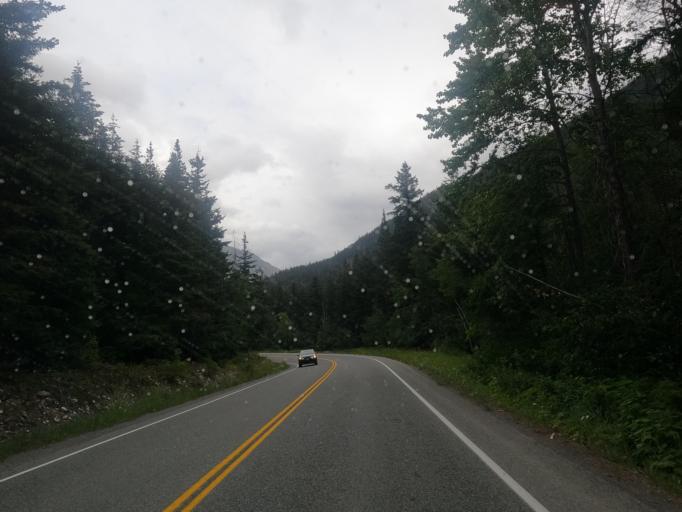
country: CA
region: British Columbia
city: Lillooet
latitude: 50.5068
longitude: -122.1734
